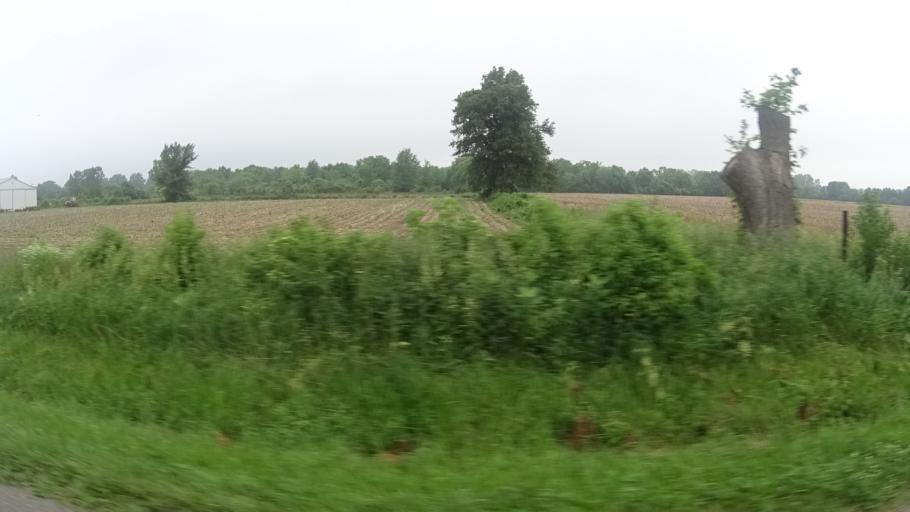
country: US
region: Ohio
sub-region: Huron County
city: Bellevue
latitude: 41.3621
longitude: -82.8041
